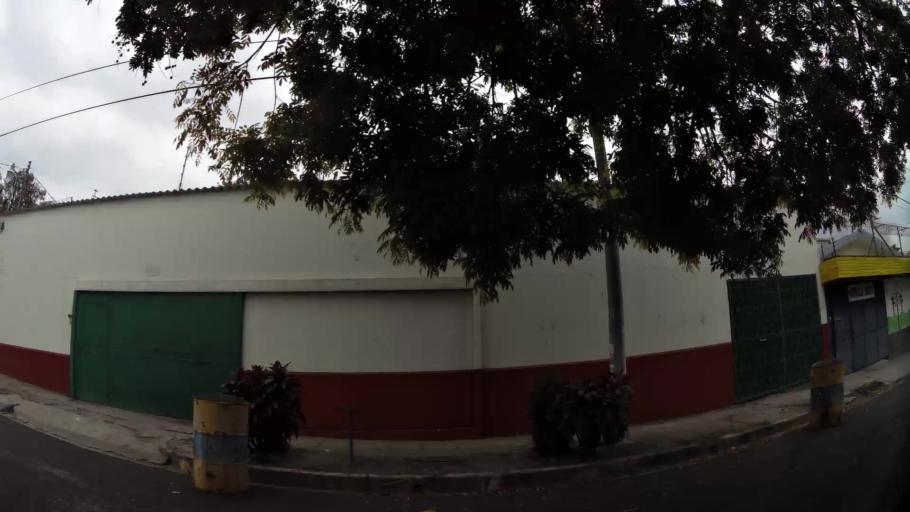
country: SV
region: San Salvador
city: Mejicanos
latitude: 13.7075
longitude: -89.2373
